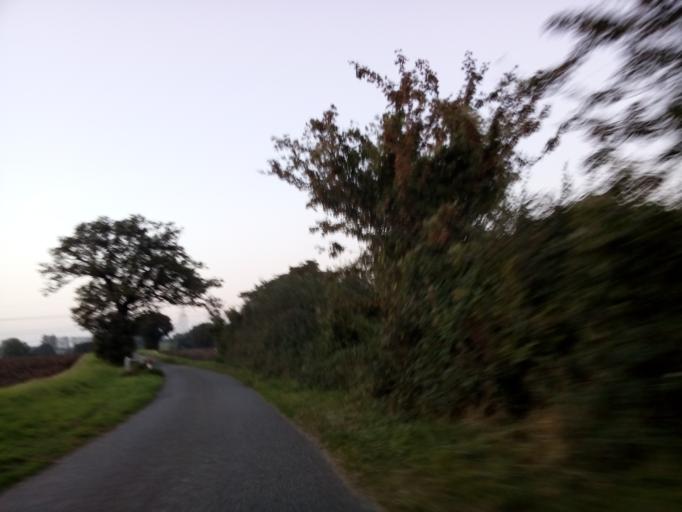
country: GB
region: England
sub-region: Suffolk
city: Kesgrave
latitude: 52.1097
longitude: 1.2343
